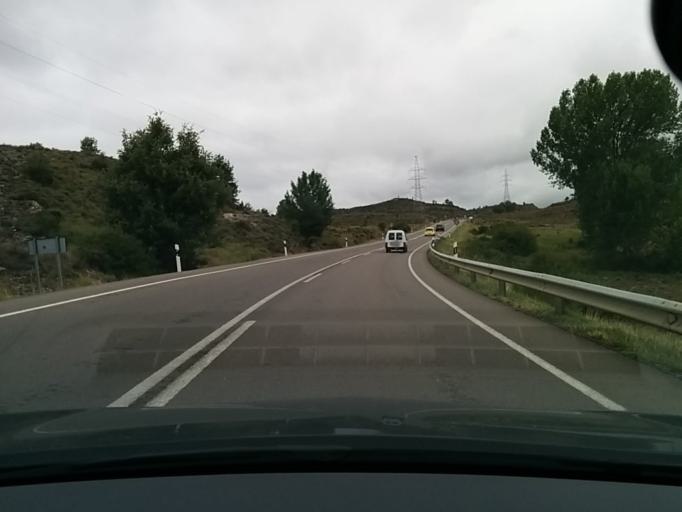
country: ES
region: Aragon
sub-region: Provincia de Huesca
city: Sabinanigo
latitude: 42.4189
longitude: -0.3953
